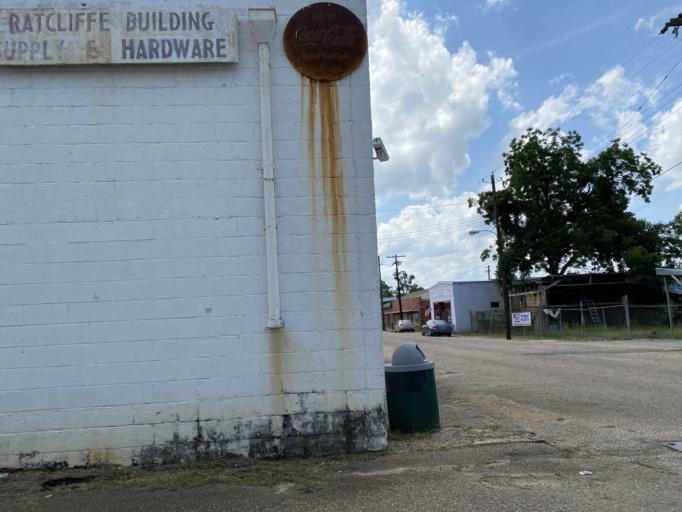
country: US
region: Alabama
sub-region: Wilcox County
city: Camden
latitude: 31.9916
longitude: -87.2904
